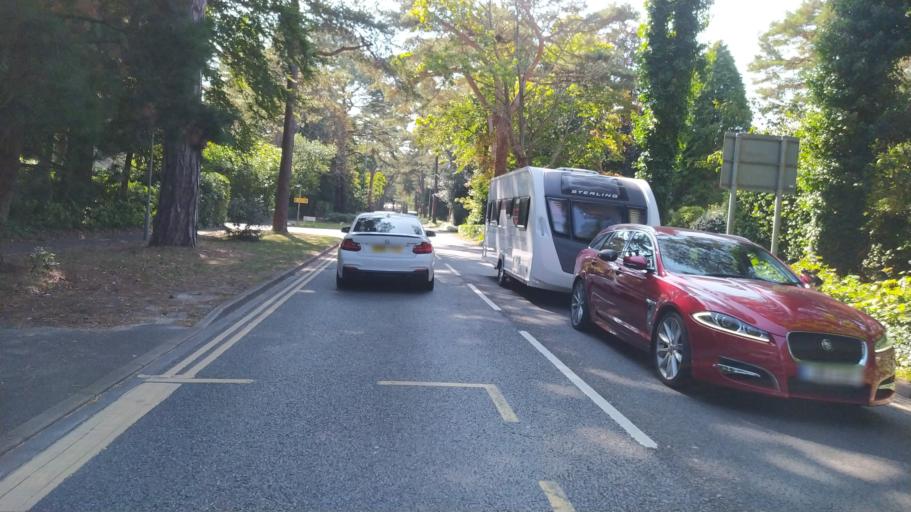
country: GB
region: England
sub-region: Bournemouth
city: Bournemouth
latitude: 50.7178
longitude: -1.9093
